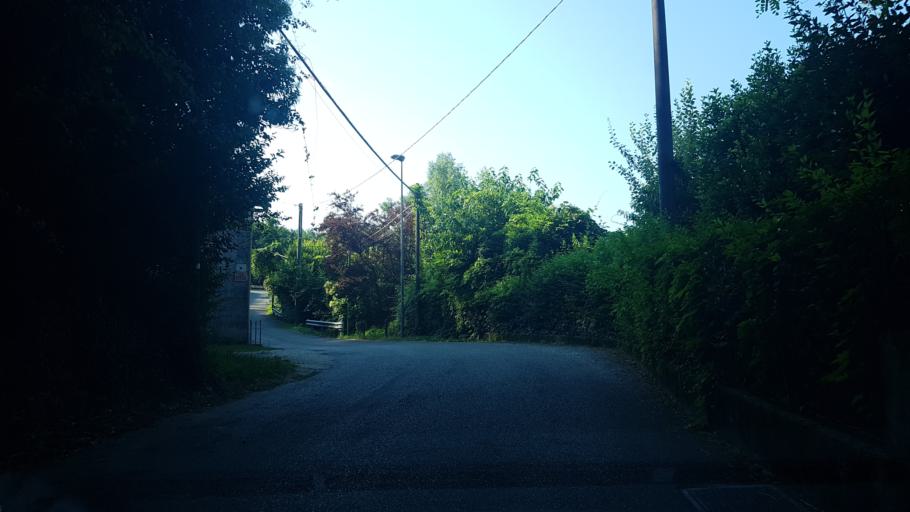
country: IT
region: Friuli Venezia Giulia
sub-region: Provincia di Udine
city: Tarcento
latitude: 46.2130
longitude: 13.2302
